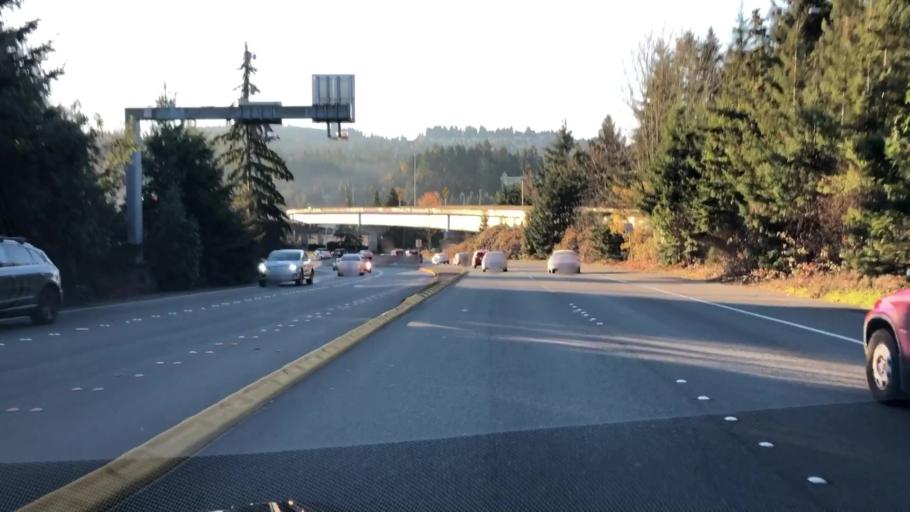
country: US
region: Washington
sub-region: King County
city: Eastgate
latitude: 47.5831
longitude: -122.1428
